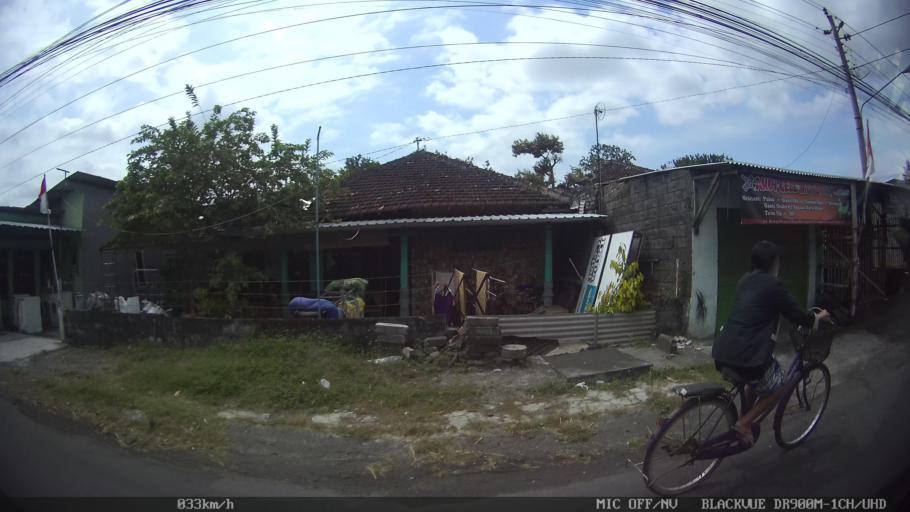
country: ID
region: Daerah Istimewa Yogyakarta
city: Depok
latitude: -7.7841
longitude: 110.4643
